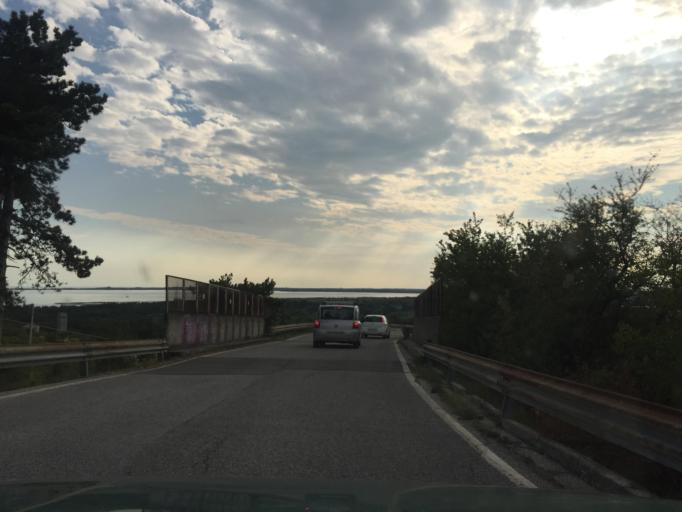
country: IT
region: Friuli Venezia Giulia
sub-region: Provincia di Trieste
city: Duino
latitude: 45.7917
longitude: 13.5961
